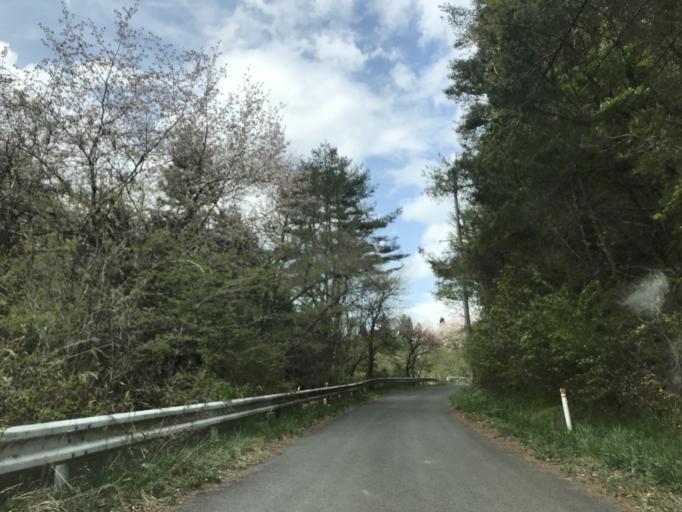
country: JP
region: Iwate
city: Ichinoseki
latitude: 38.7812
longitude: 141.4312
